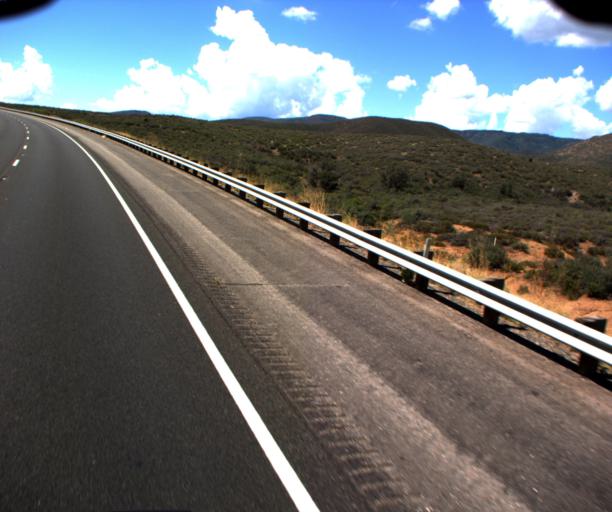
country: US
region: Arizona
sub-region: Yavapai County
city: Mayer
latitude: 34.4581
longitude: -112.2726
